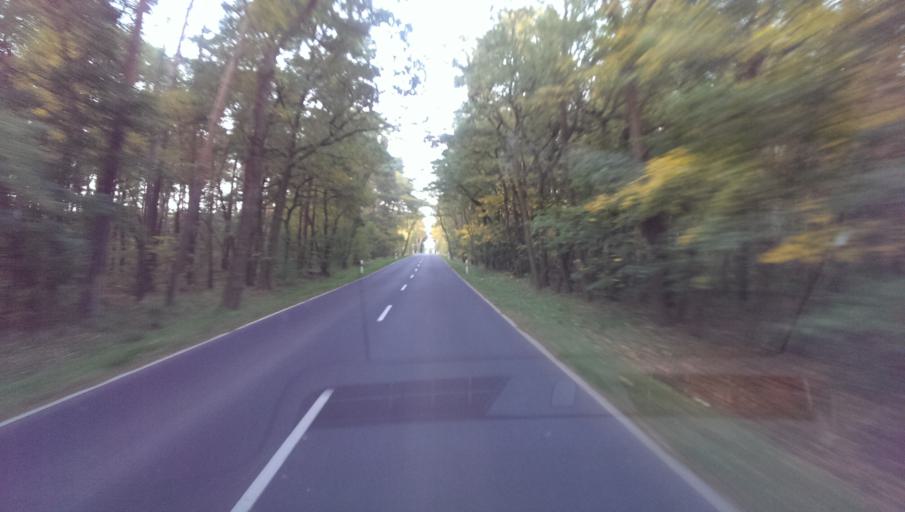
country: DE
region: Saxony-Anhalt
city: Jessen
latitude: 51.8299
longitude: 13.0167
